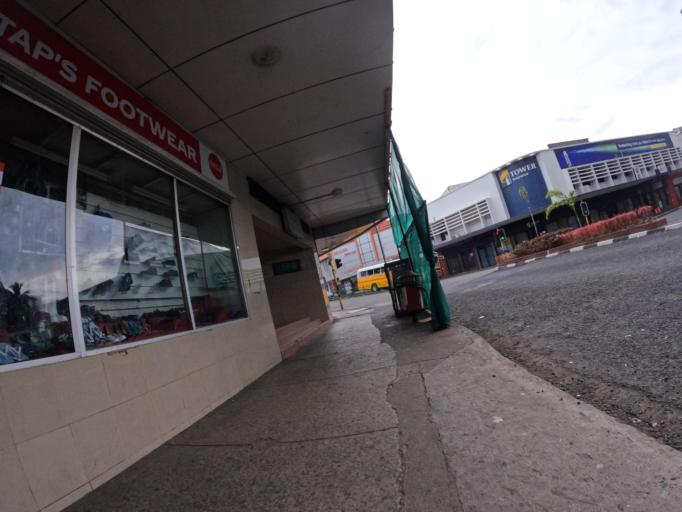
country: FJ
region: Central
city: Suva
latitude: -18.1373
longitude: 178.4258
